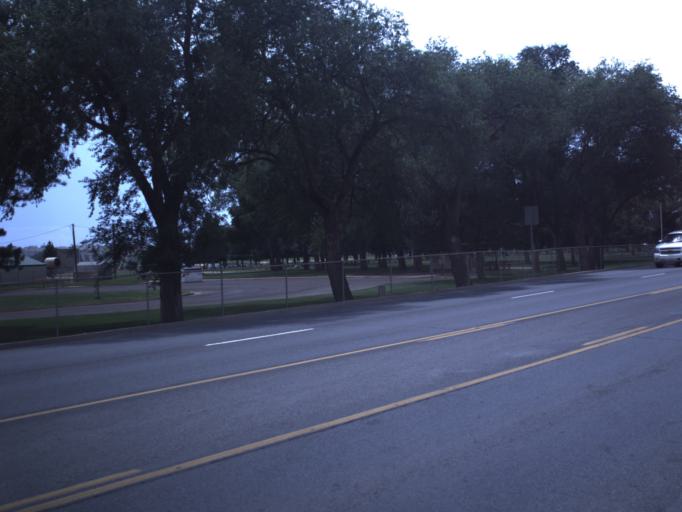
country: US
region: Utah
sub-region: Duchesne County
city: Roosevelt
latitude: 40.2901
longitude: -109.9980
